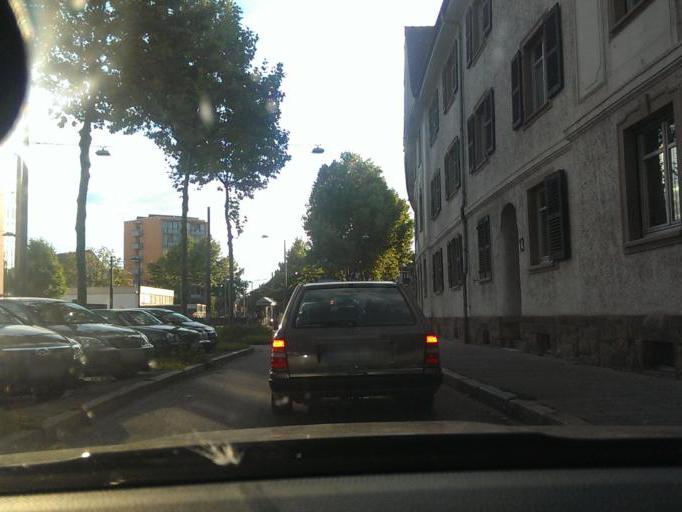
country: DE
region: Baden-Wuerttemberg
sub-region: Karlsruhe Region
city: Karlsruhe
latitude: 48.9983
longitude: 8.4627
